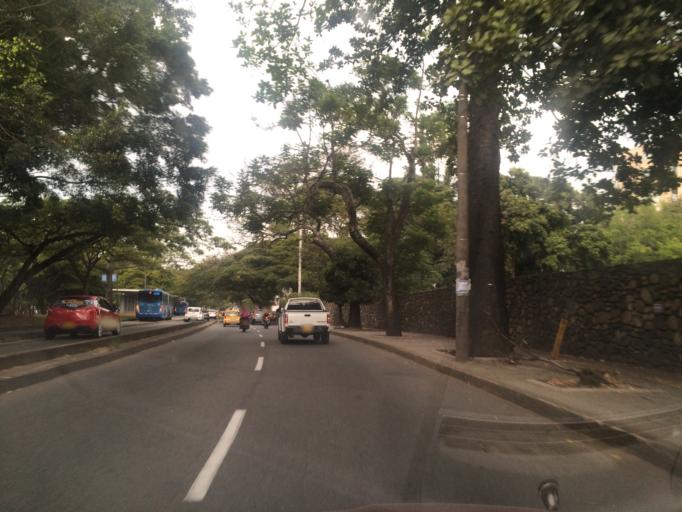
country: CO
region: Valle del Cauca
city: Cali
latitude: 3.3732
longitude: -76.5413
